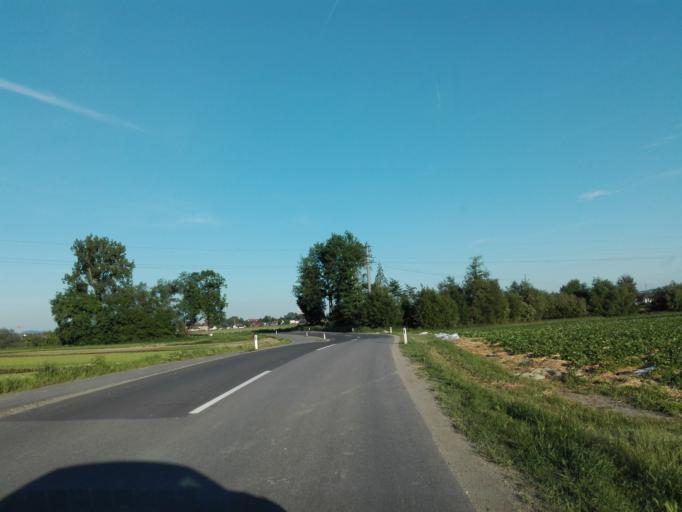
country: AT
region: Upper Austria
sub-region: Politischer Bezirk Urfahr-Umgebung
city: Feldkirchen an der Donau
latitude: 48.3187
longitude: 14.0001
